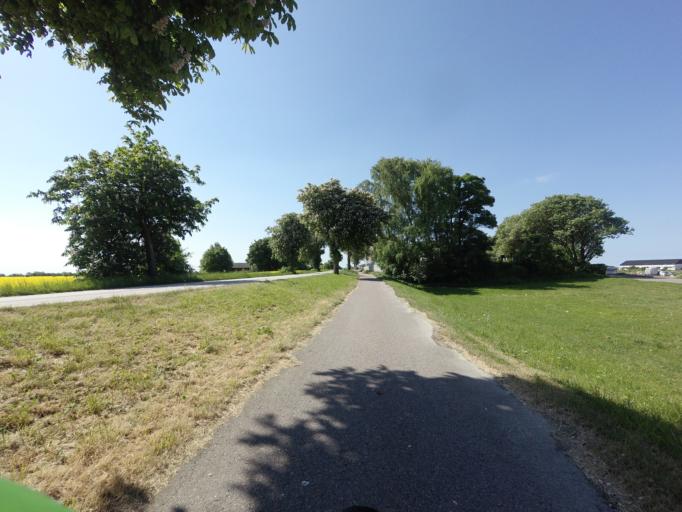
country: SE
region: Skane
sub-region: Vellinge Kommun
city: Vellinge
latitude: 55.4536
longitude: 12.9894
